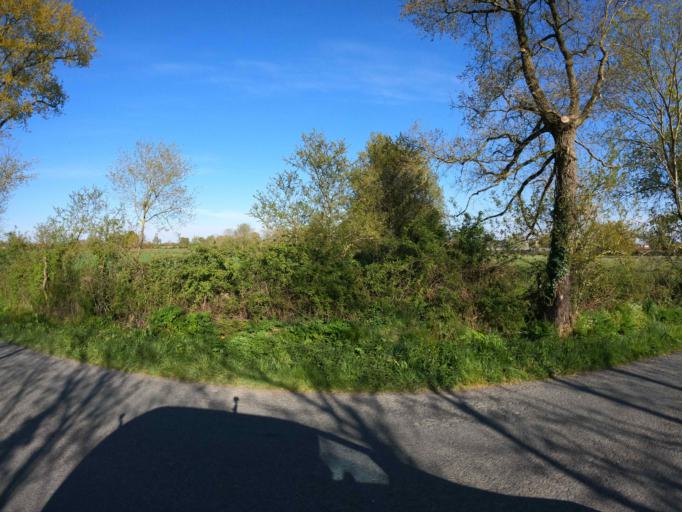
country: FR
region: Pays de la Loire
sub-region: Departement de la Vendee
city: Beaurepaire
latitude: 46.9243
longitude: -1.1163
